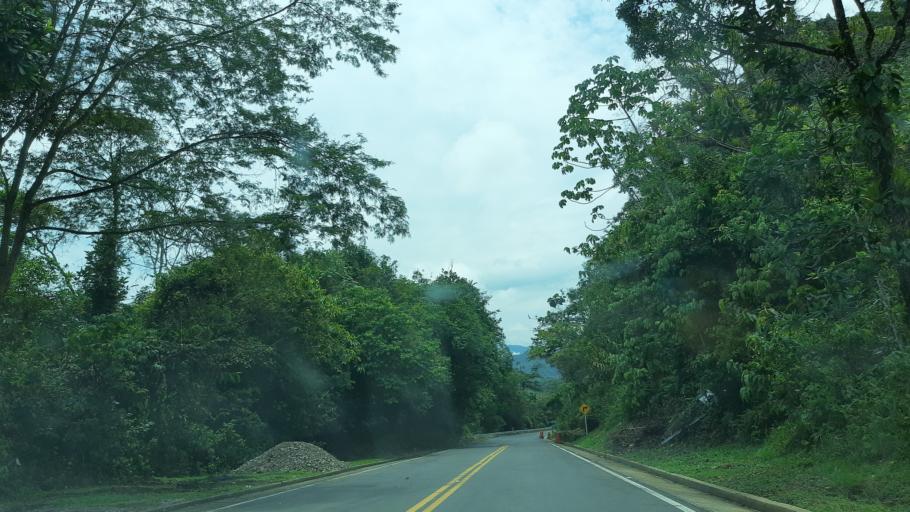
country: CO
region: Boyaca
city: San Luis de Gaceno
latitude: 4.8289
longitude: -73.1485
